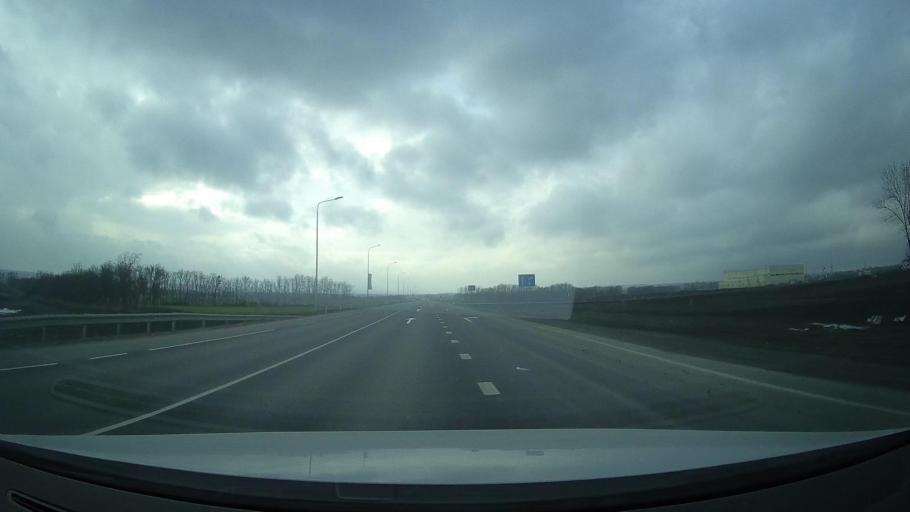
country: RU
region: Rostov
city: Grushevskaya
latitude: 47.4753
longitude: 39.9133
